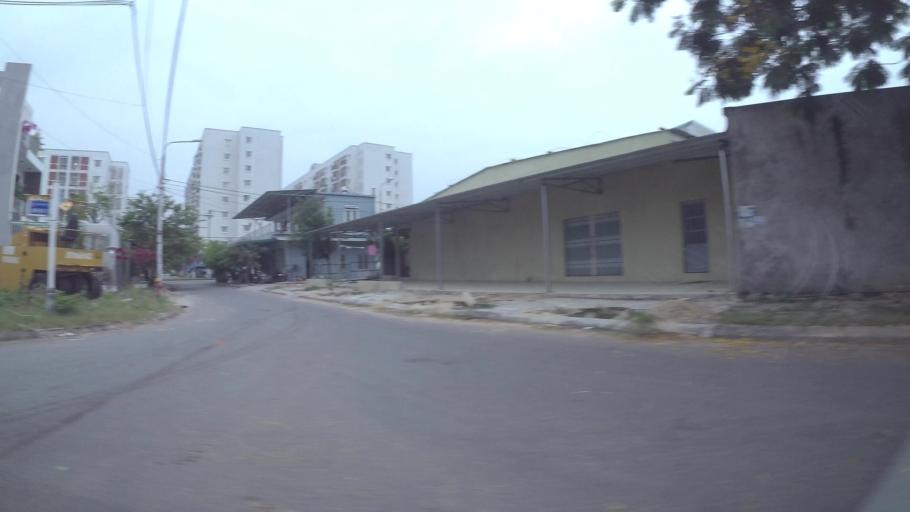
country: VN
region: Da Nang
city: Thanh Khe
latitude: 16.0453
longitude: 108.1766
